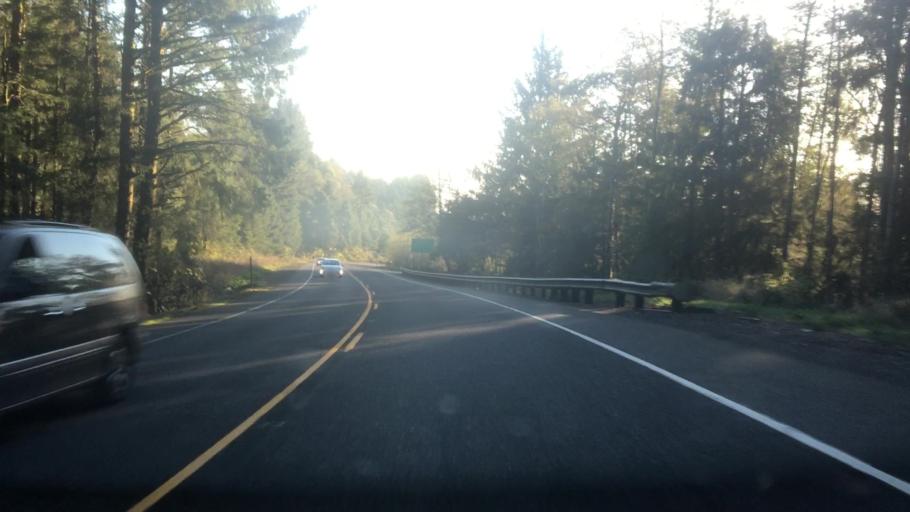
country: US
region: Oregon
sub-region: Clatsop County
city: Cannon Beach
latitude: 45.9120
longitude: -123.9486
